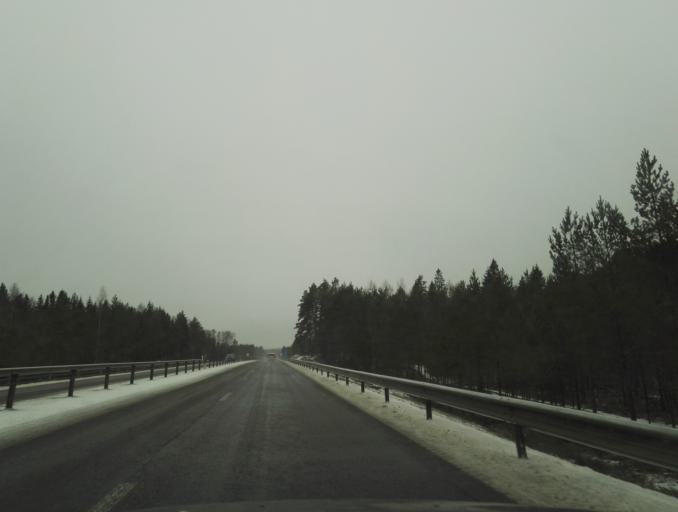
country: SE
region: Kronoberg
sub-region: Alvesta Kommun
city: Vislanda
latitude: 56.7252
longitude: 14.4676
